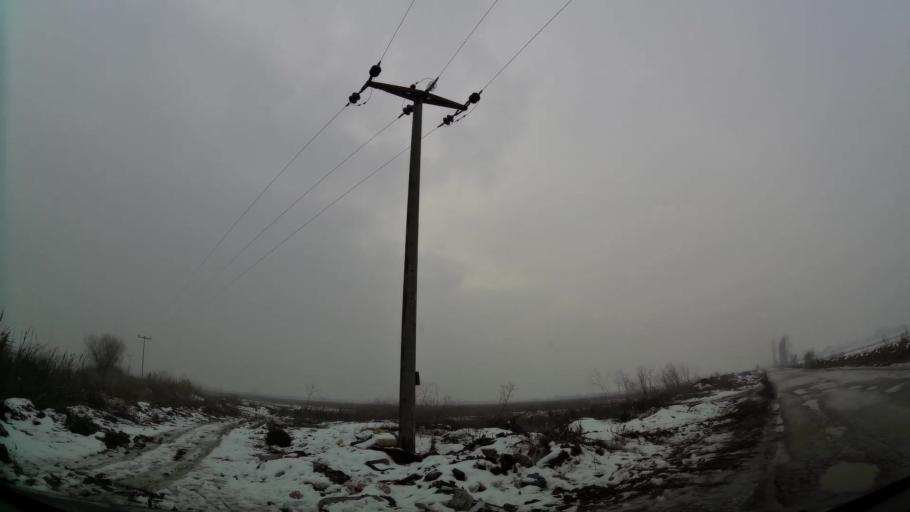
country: MK
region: Petrovec
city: Petrovec
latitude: 41.9332
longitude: 21.6075
